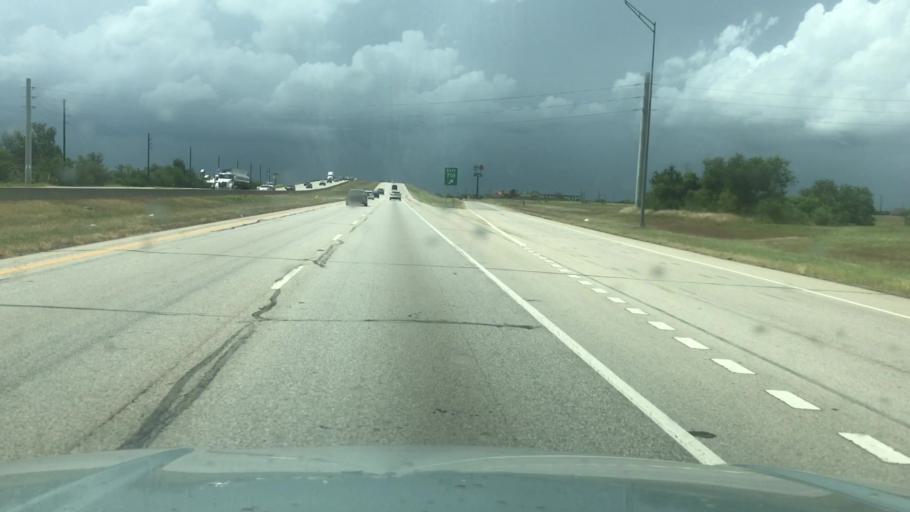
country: US
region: Texas
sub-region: Austin County
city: Sealy
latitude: 29.7612
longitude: -96.1791
